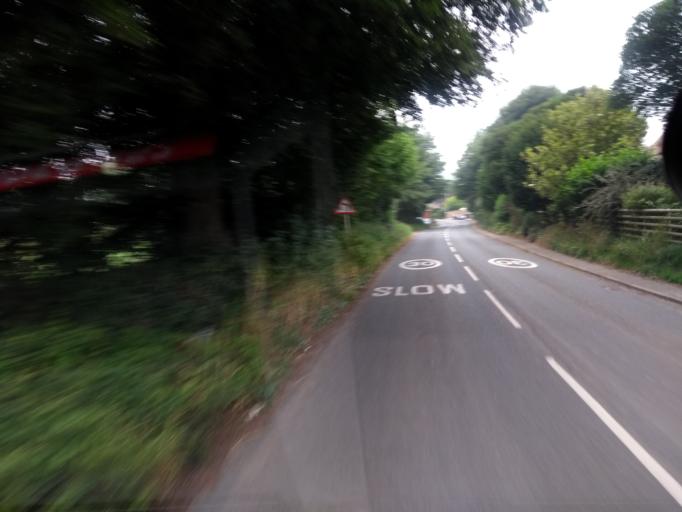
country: GB
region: England
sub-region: Dorset
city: Bridport
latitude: 50.7347
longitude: -2.7724
